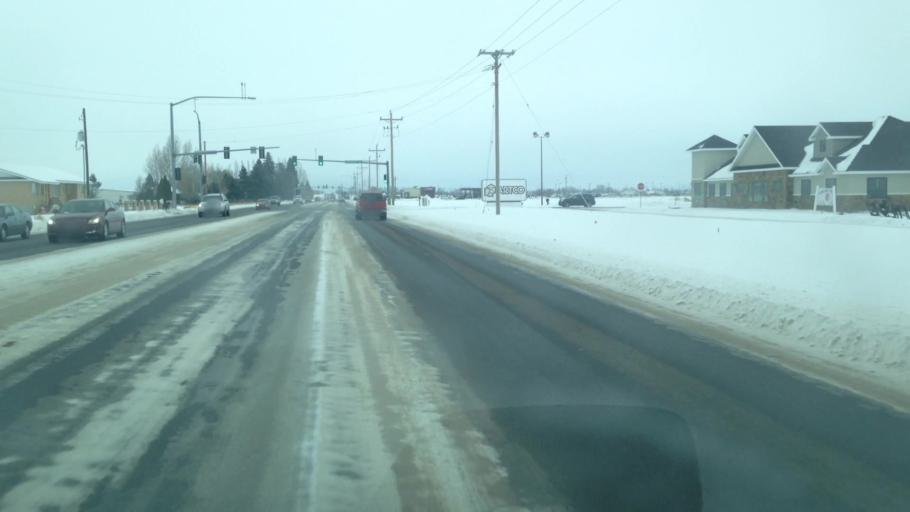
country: US
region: Idaho
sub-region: Madison County
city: Rexburg
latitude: 43.8508
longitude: -111.7779
